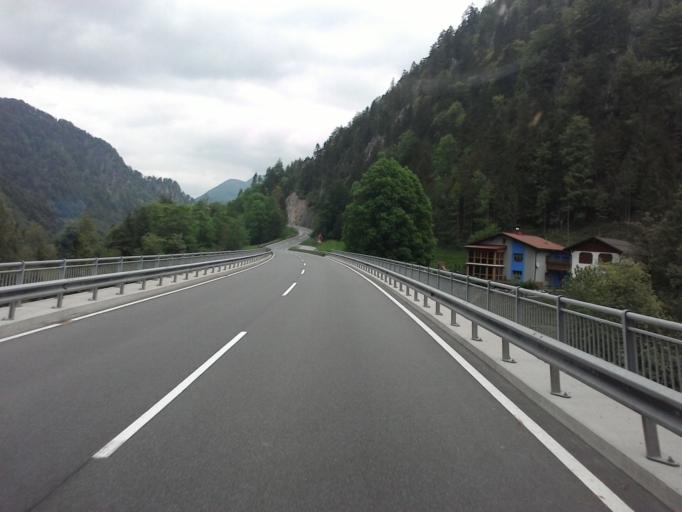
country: AT
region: Styria
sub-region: Politischer Bezirk Liezen
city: Altenmarkt bei Sankt Gallen
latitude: 47.7515
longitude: 14.6447
